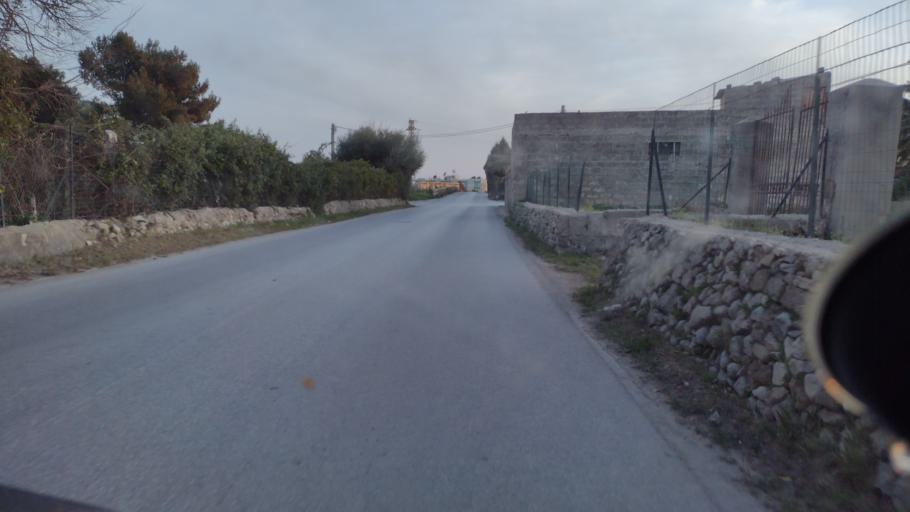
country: IT
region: Sicily
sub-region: Provincia di Siracusa
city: Avola
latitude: 36.8986
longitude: 15.1344
